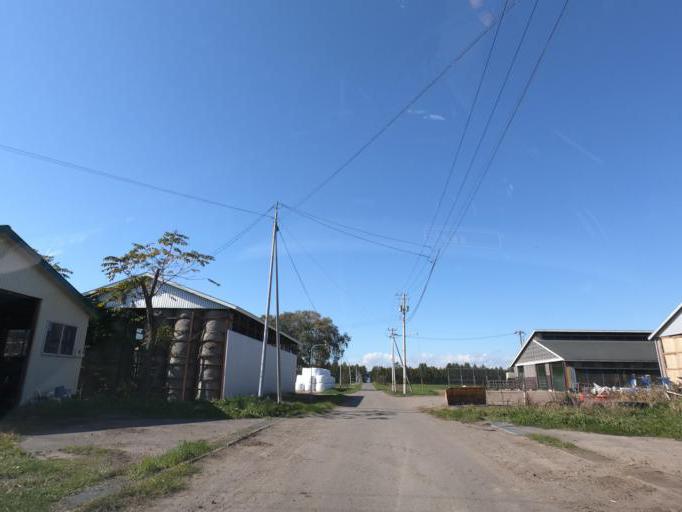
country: JP
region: Hokkaido
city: Otofuke
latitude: 43.0703
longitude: 143.2709
